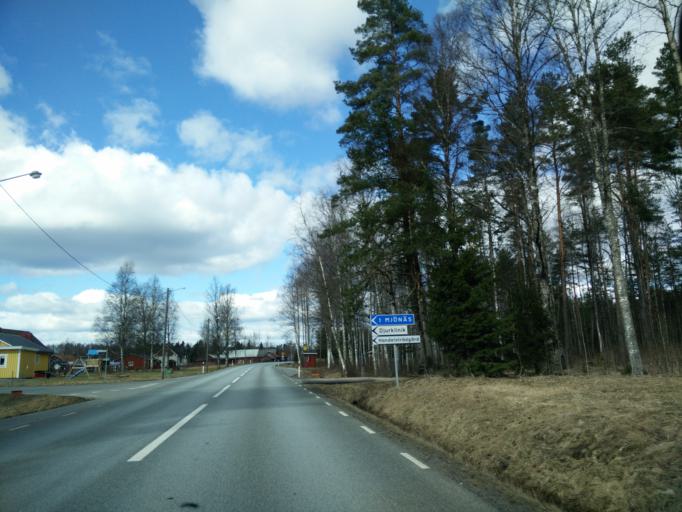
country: SE
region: Vaermland
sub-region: Munkfors Kommun
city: Munkfors
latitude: 59.8736
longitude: 13.5609
